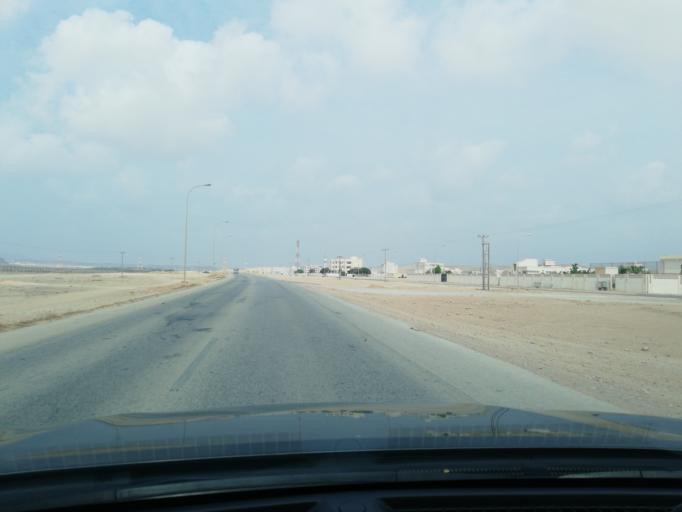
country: OM
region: Zufar
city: Salalah
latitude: 16.9491
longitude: 53.9712
